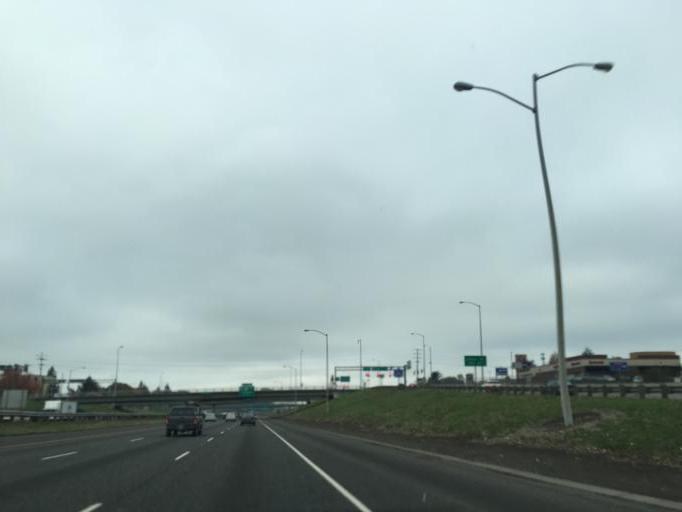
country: US
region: Oregon
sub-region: Multnomah County
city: Lents
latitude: 45.5166
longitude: -122.5653
